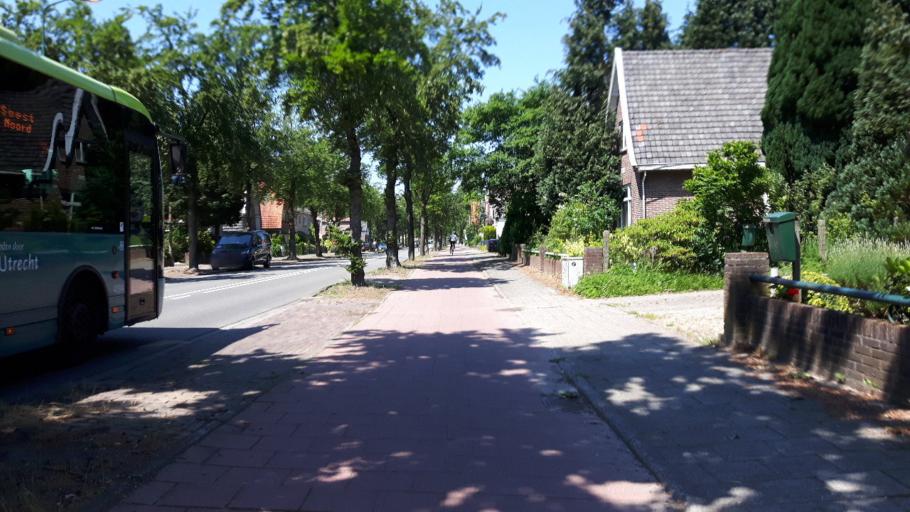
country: NL
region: Utrecht
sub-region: Gemeente Soest
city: Soest
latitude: 52.1692
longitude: 5.2962
